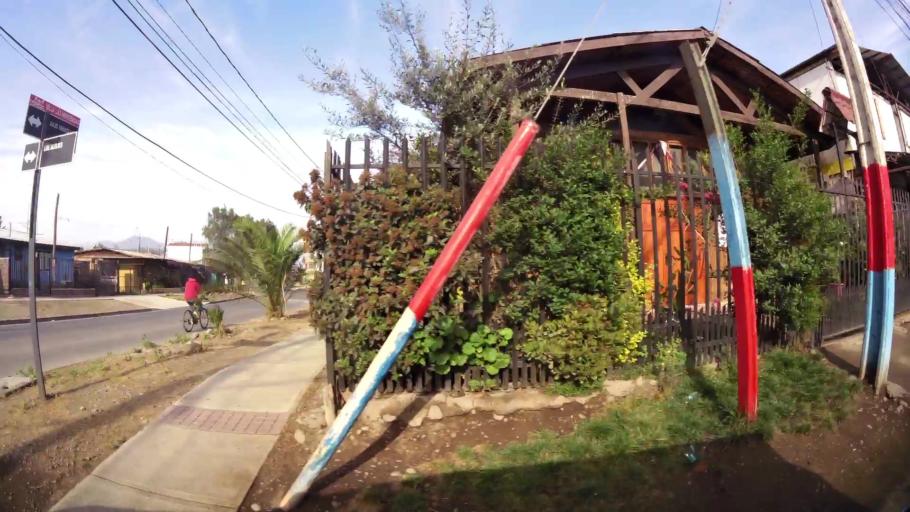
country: CL
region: Santiago Metropolitan
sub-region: Provincia de Talagante
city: Talagante
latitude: -33.6700
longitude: -70.9354
